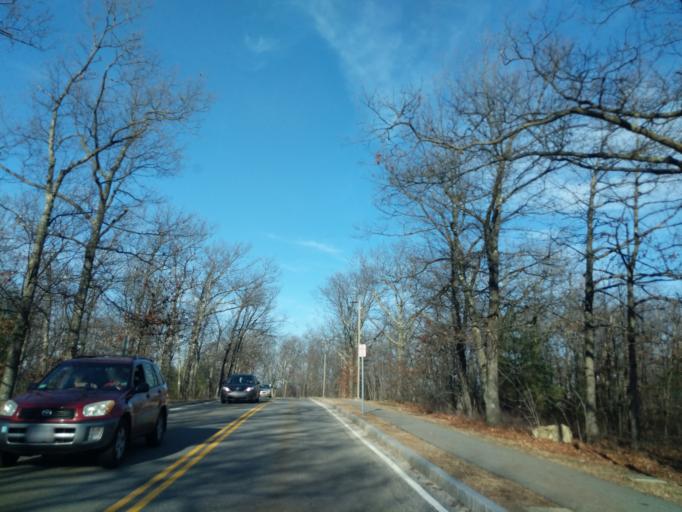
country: US
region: Massachusetts
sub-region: Worcester County
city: Hamilton
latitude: 42.2820
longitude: -71.7758
